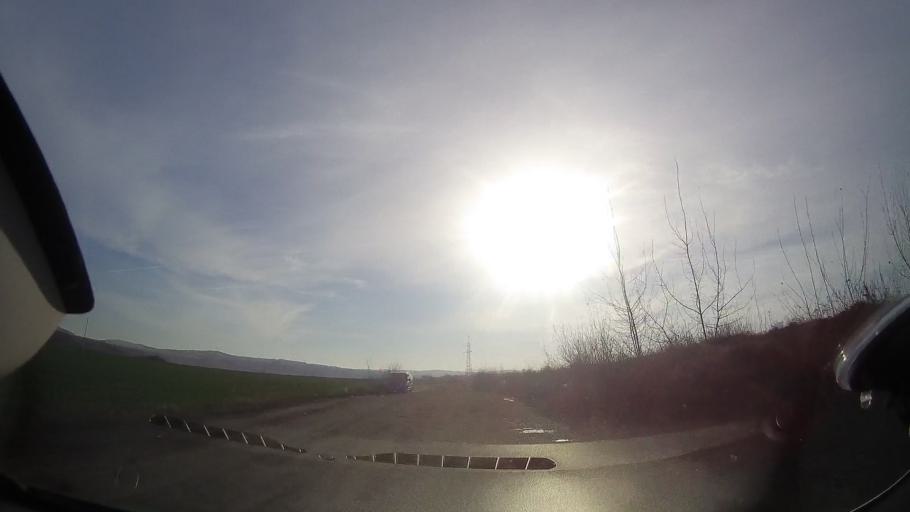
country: RO
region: Bihor
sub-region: Comuna Ciuhoiu
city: Ciuhoiu
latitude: 47.2179
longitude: 22.1346
